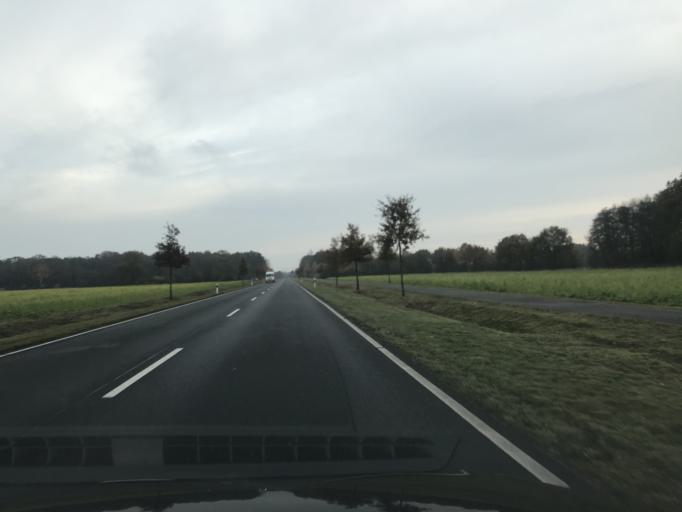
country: DE
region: North Rhine-Westphalia
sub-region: Regierungsbezirk Munster
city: Ladbergen
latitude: 52.1211
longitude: 7.6959
